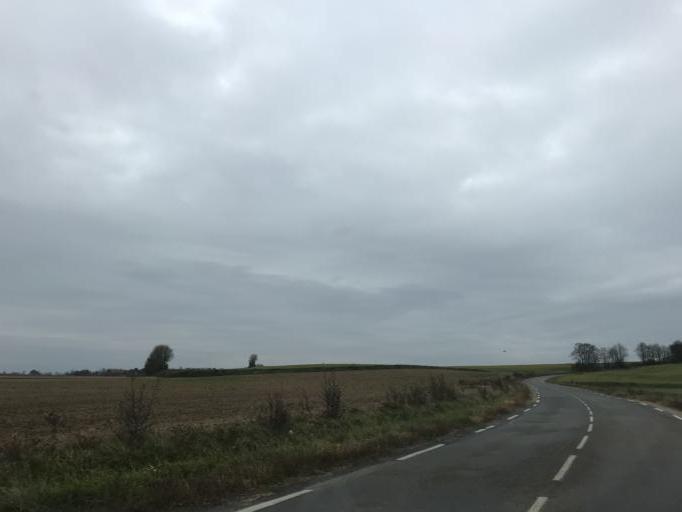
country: FR
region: Rhone-Alpes
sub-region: Departement de l'Ain
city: Miribel
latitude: 45.8432
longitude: 4.9545
